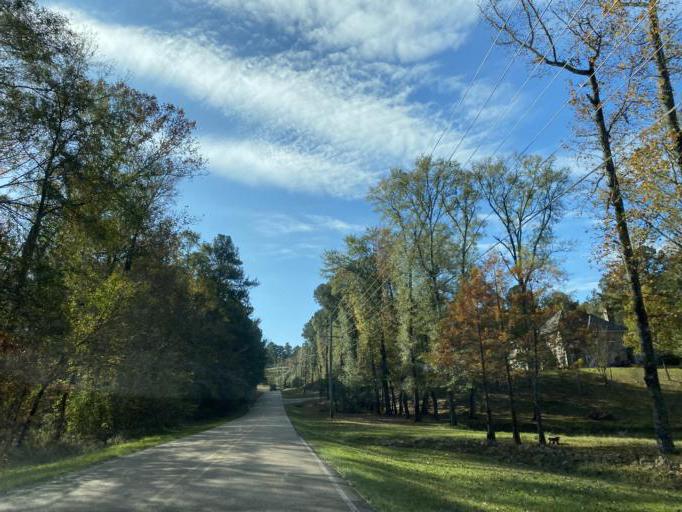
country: US
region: Mississippi
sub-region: Madison County
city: Ridgeland
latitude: 32.4628
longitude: -90.1855
